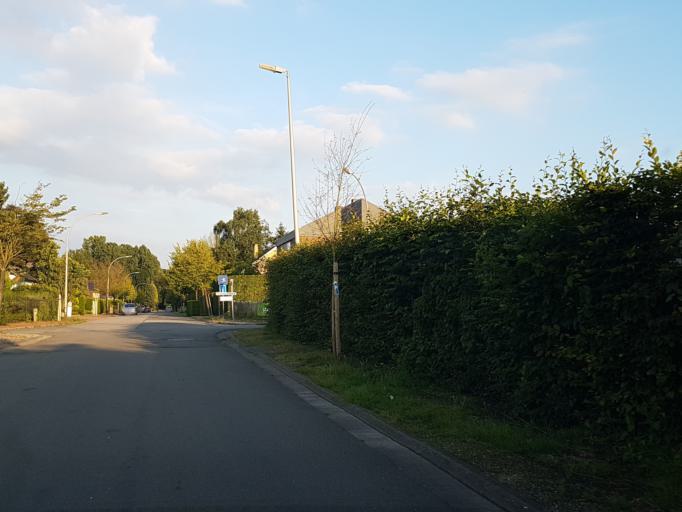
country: BE
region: Flanders
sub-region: Provincie Vlaams-Brabant
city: Dilbeek
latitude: 50.8497
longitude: 4.2380
